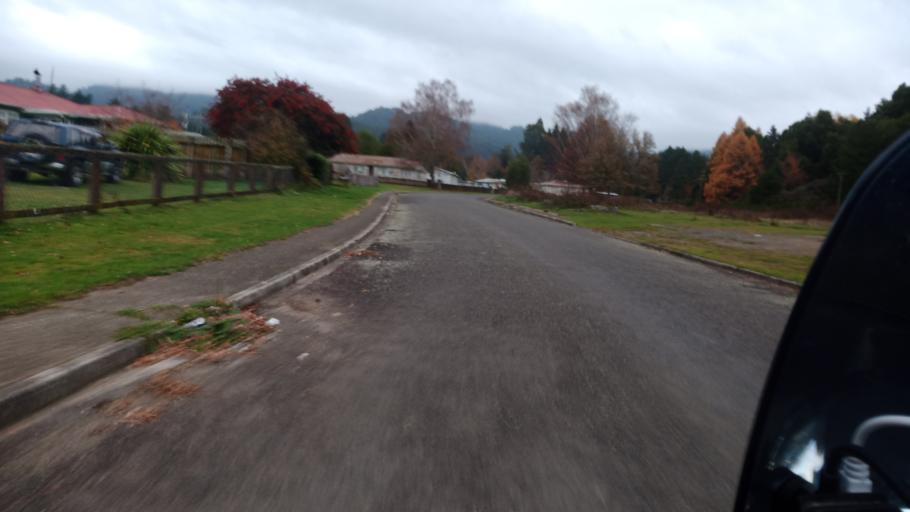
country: NZ
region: Bay of Plenty
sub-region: Whakatane District
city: Murupara
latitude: -38.6422
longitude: 176.7305
